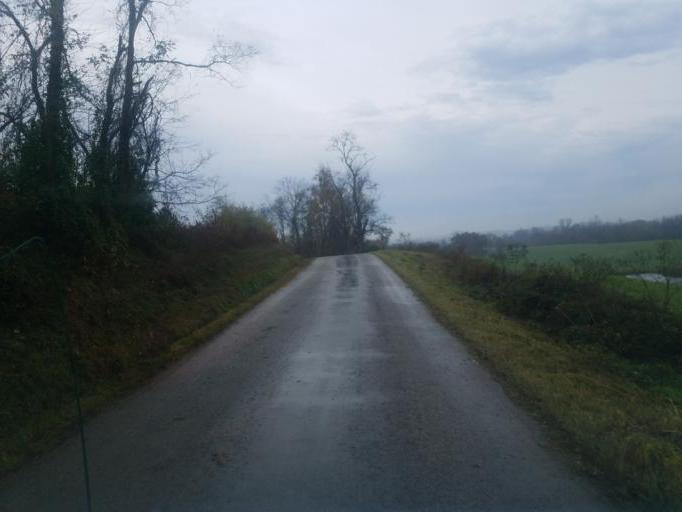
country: US
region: Ohio
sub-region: Morgan County
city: McConnelsville
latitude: 39.5129
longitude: -81.8312
